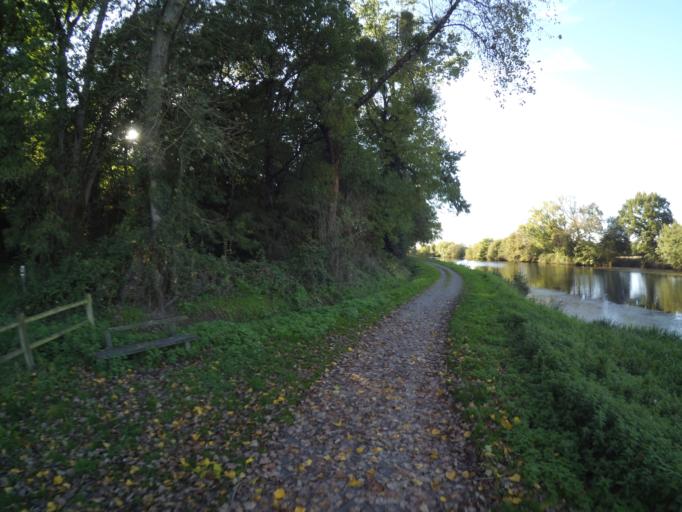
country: FR
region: Brittany
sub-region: Departement du Morbihan
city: Peillac
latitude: 47.7230
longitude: -2.1959
